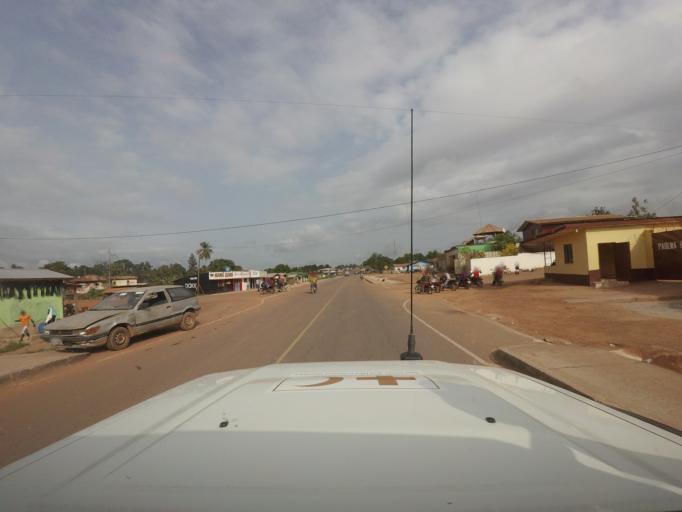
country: LR
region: Bong
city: Gbarnga
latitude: 6.9999
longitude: -9.4723
